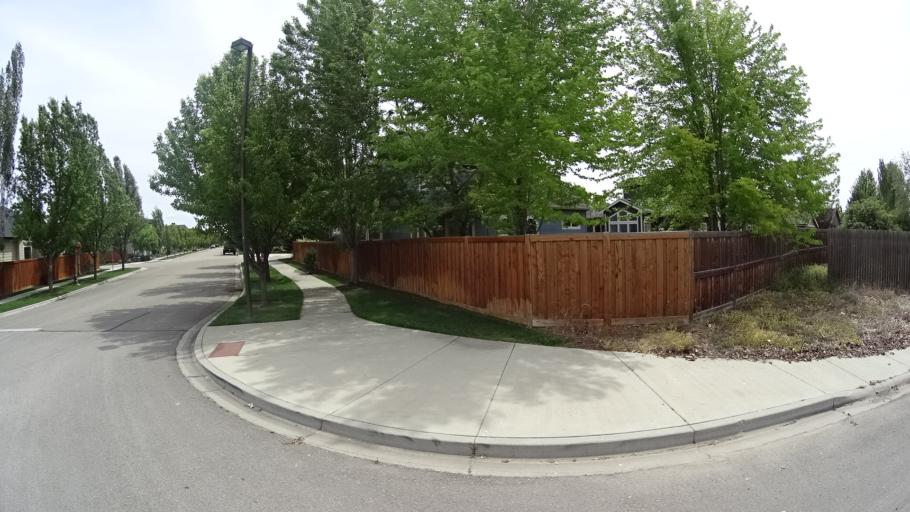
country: US
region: Idaho
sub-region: Ada County
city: Meridian
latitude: 43.5441
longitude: -116.3244
